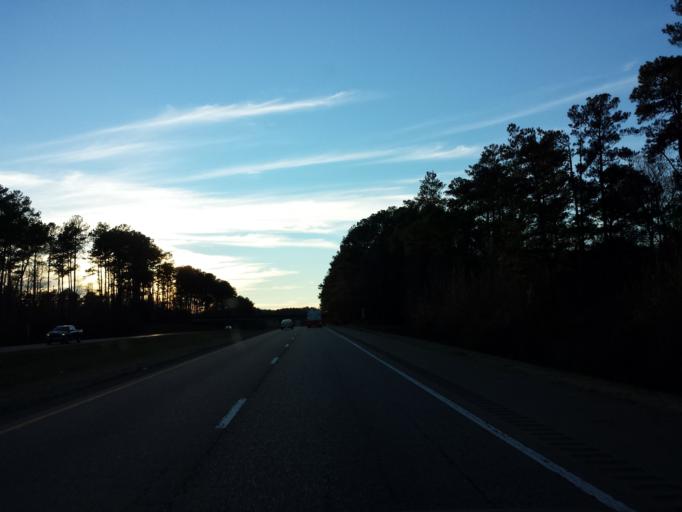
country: US
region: Mississippi
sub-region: Lauderdale County
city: Marion
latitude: 32.3920
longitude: -88.5928
